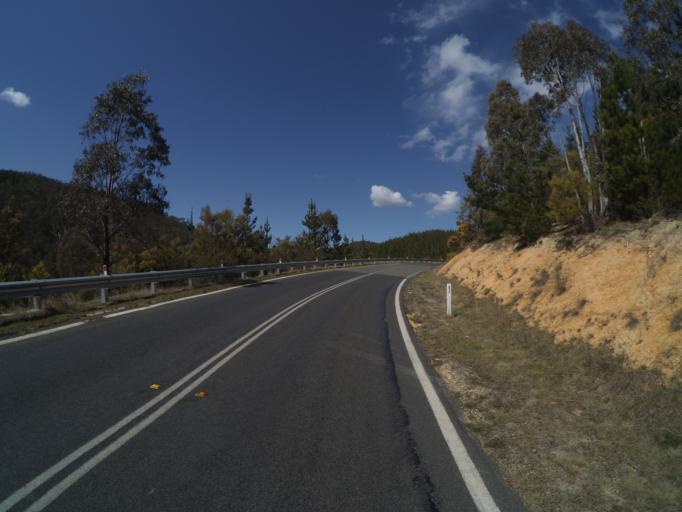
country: AU
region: Australian Capital Territory
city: Macquarie
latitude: -35.3684
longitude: 148.9608
